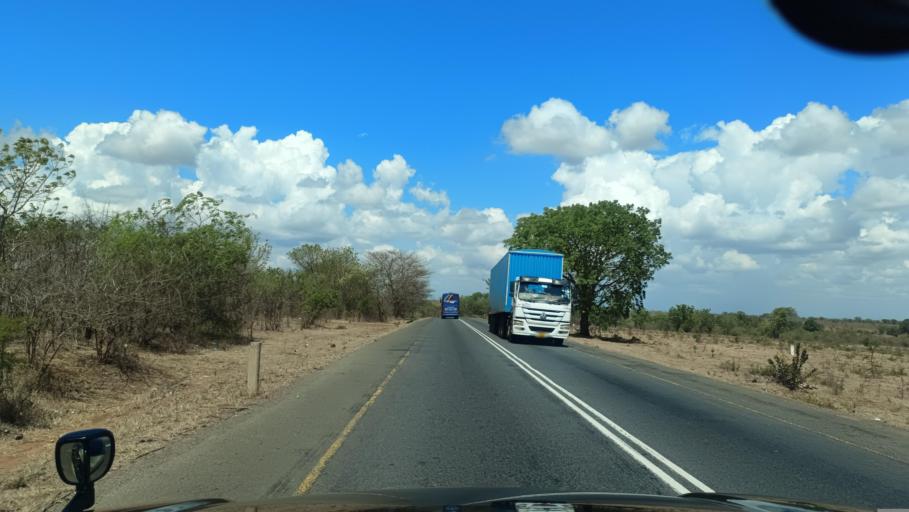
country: TZ
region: Morogoro
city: Morogoro
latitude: -6.9062
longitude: 37.4801
